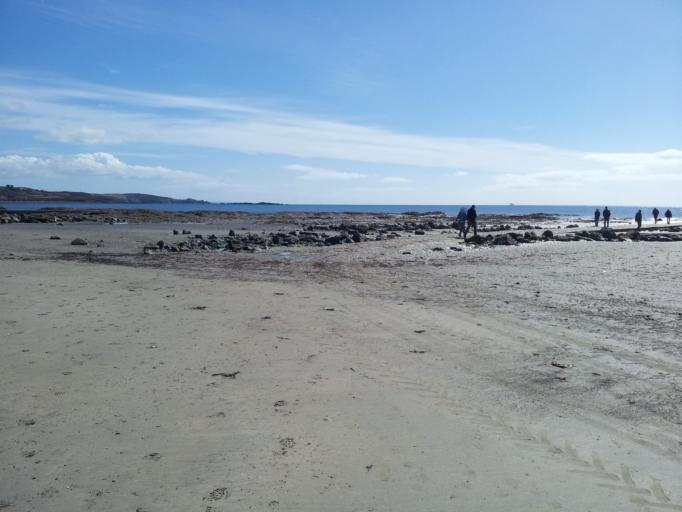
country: GB
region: England
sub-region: Cornwall
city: Marazion
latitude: 50.1231
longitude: -5.4752
